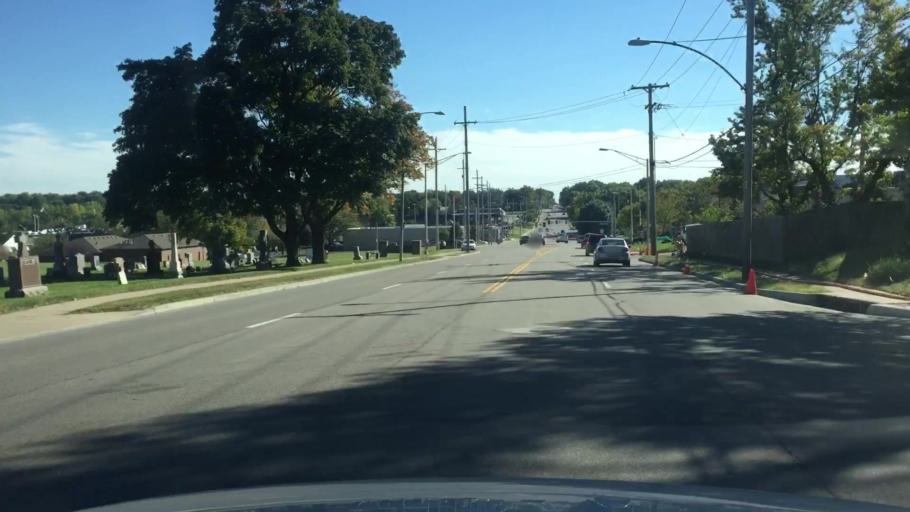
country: US
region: Kansas
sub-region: Johnson County
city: Shawnee
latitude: 39.0173
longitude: -94.7239
